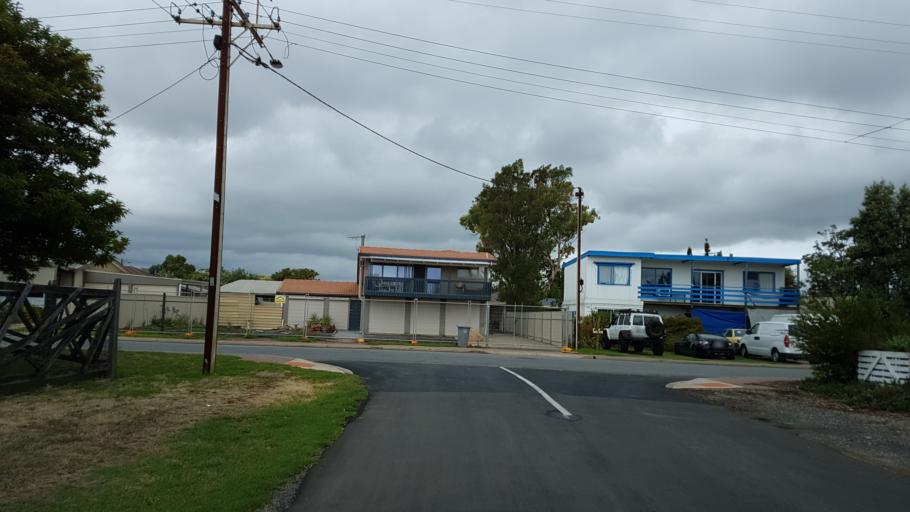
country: AU
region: South Australia
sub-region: Onkaparinga
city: Port Willunga
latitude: -35.2763
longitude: 138.4452
